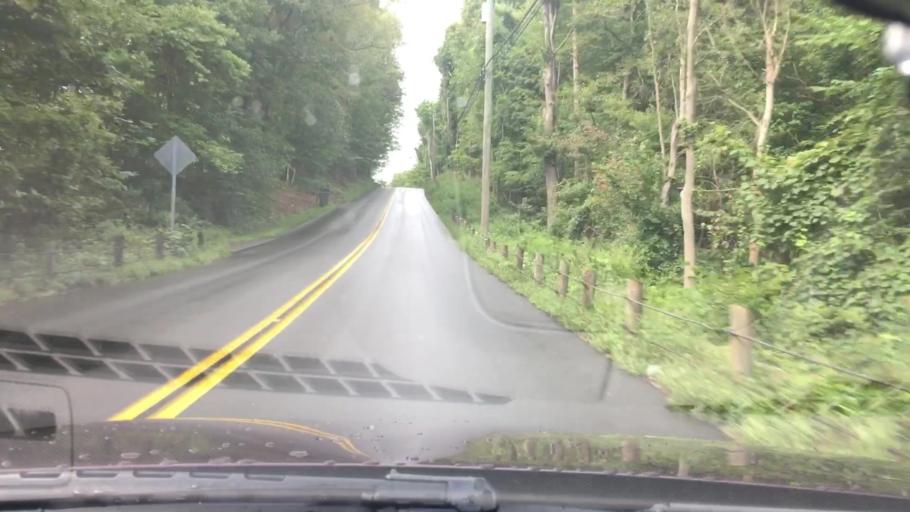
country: US
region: Connecticut
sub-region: Hartford County
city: Manchester
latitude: 41.7340
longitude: -72.5356
